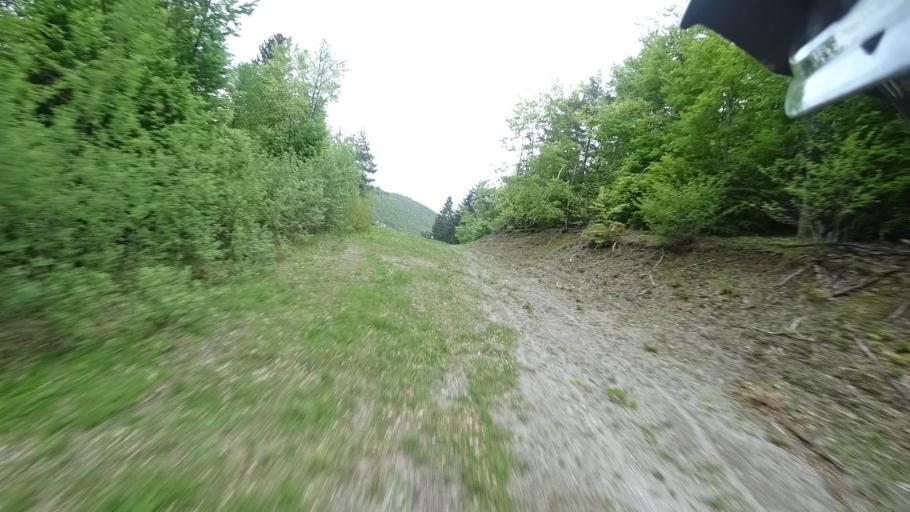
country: HR
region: Licko-Senjska
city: Jezerce
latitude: 44.8795
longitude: 15.4330
